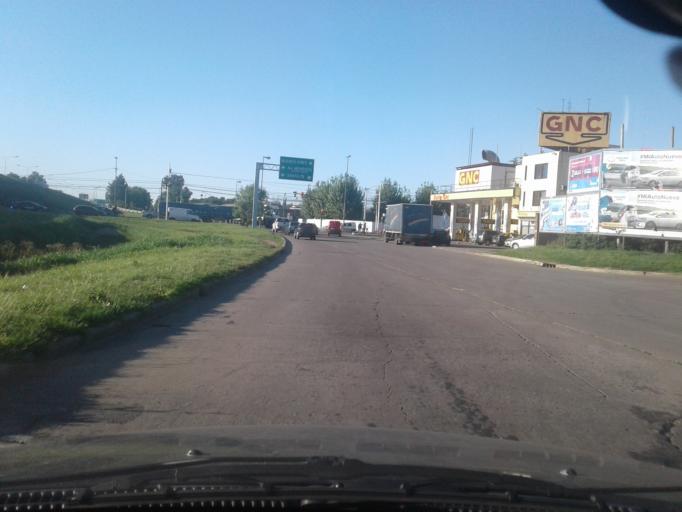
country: AR
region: Santa Fe
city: Perez
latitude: -32.9396
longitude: -60.7231
